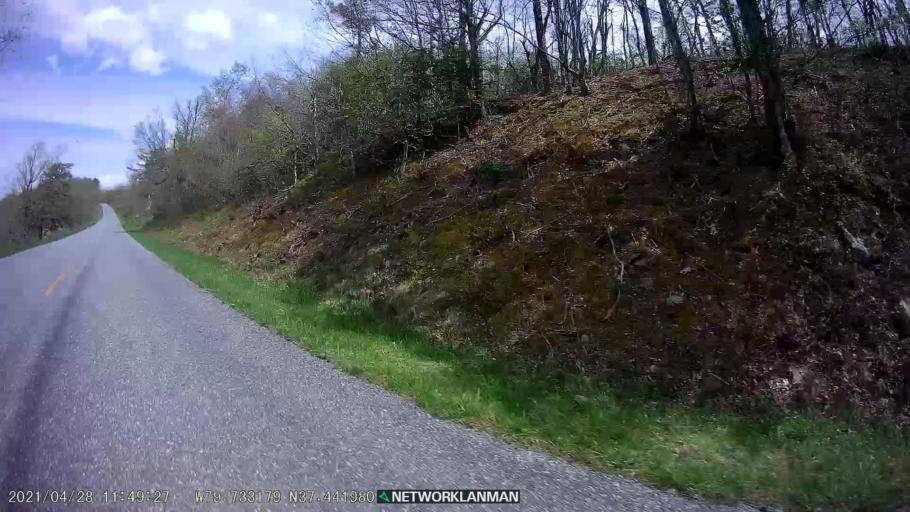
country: US
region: Virginia
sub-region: Botetourt County
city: Blue Ridge
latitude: 37.4421
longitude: -79.7330
